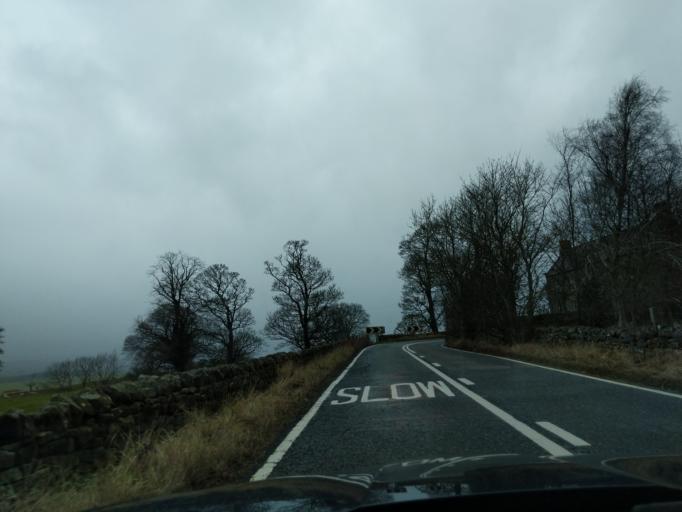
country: GB
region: England
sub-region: Northumberland
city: Otterburn
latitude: 55.2254
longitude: -2.1544
